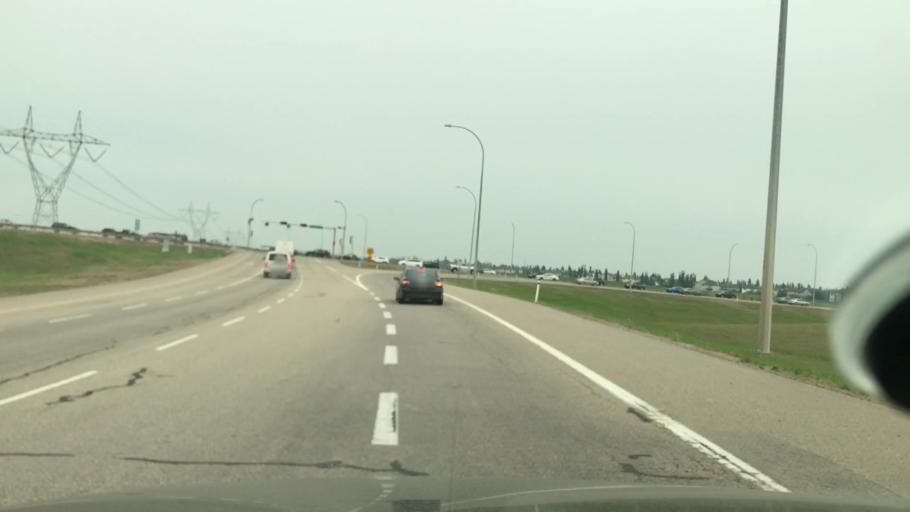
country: CA
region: Alberta
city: Devon
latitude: 53.4435
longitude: -113.5972
